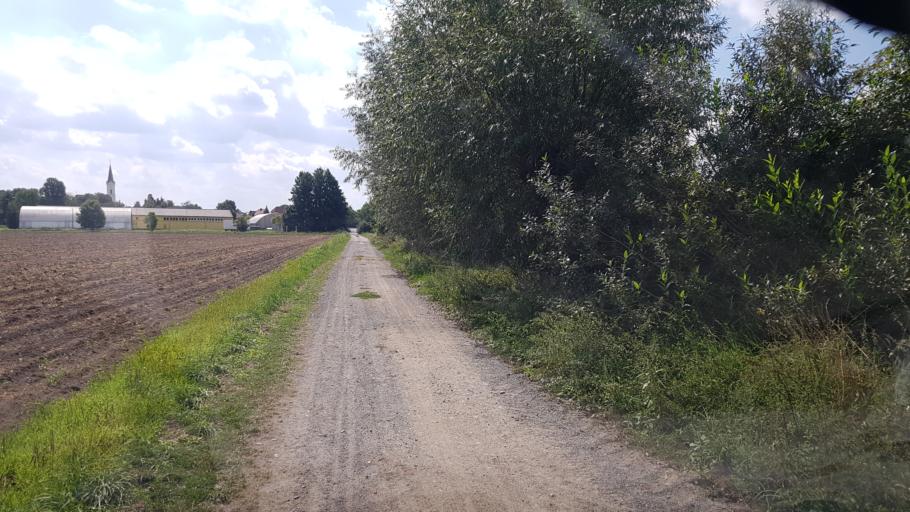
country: DE
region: Brandenburg
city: Lubbenau
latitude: 51.8680
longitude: 13.9280
